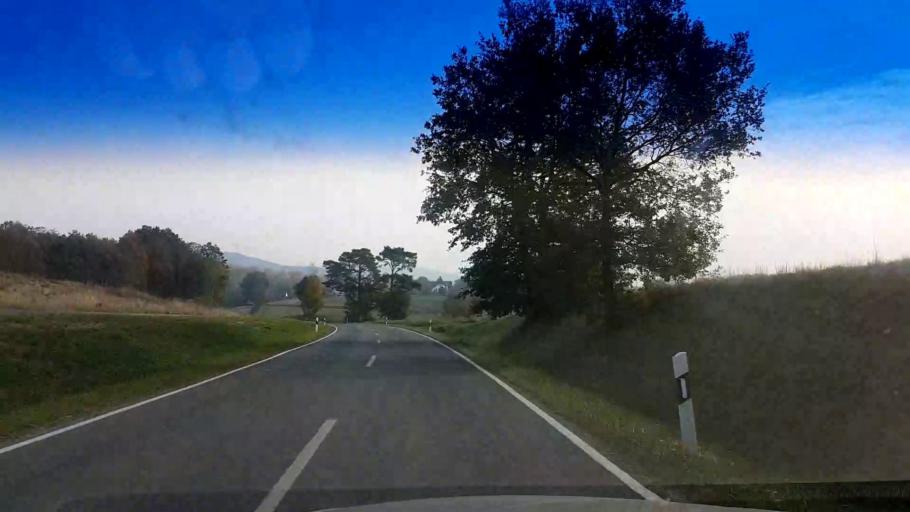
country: DE
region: Bavaria
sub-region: Upper Franconia
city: Altenkunstadt
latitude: 50.1165
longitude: 11.2883
